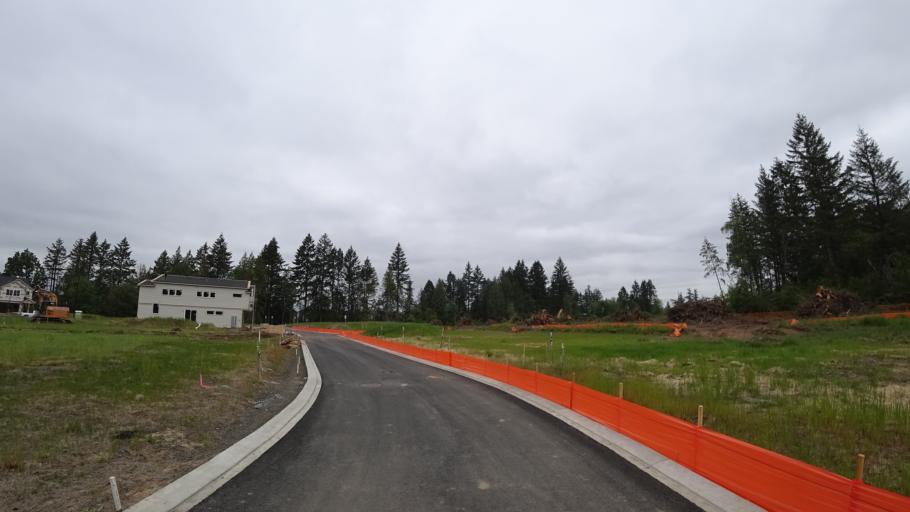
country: US
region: Oregon
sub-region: Washington County
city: Aloha
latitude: 45.4923
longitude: -122.9178
